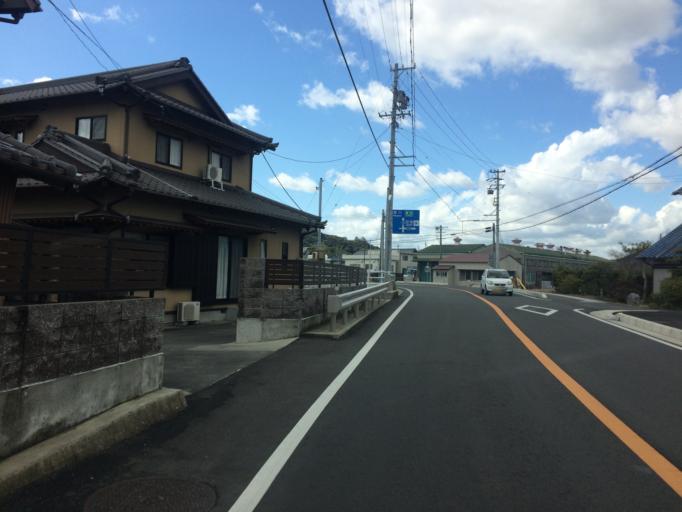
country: JP
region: Shizuoka
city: Shimada
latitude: 34.7771
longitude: 138.2139
